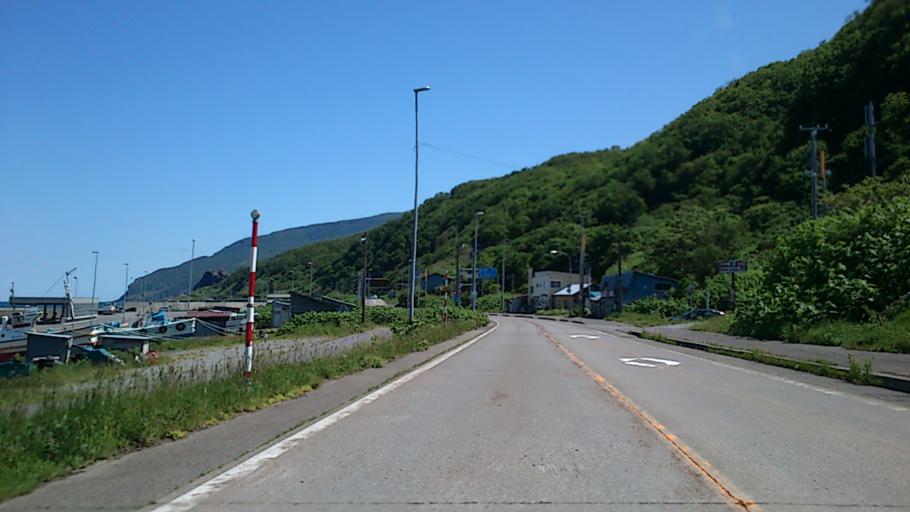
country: JP
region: Hokkaido
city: Rumoi
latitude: 43.7405
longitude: 141.3407
